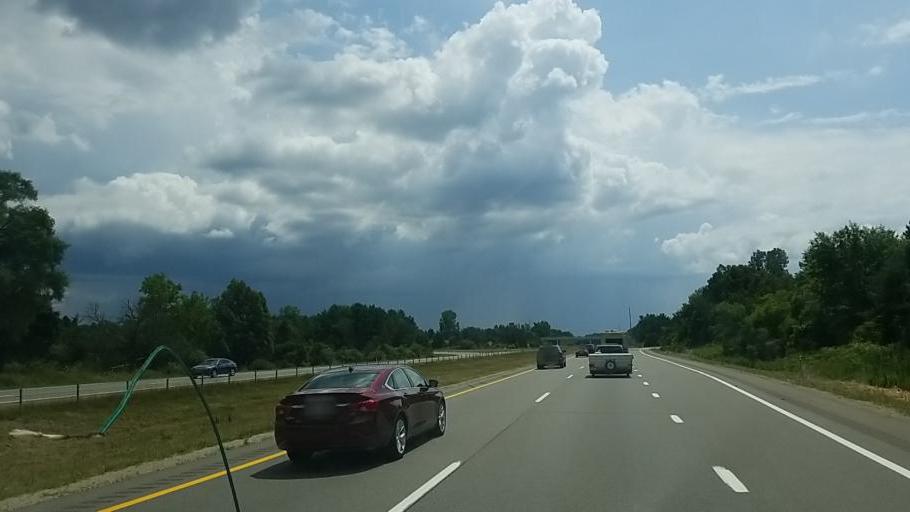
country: US
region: Michigan
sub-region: Kent County
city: East Grand Rapids
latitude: 42.9895
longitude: -85.6050
